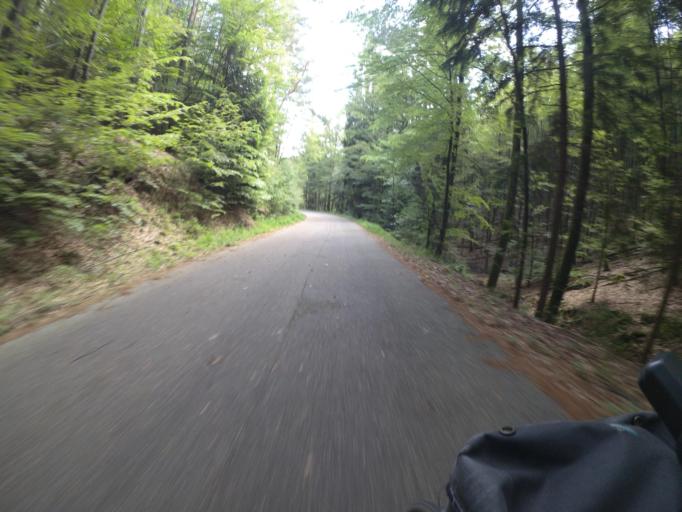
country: DE
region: Rheinland-Pfalz
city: Lemberg
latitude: 49.1450
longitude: 7.7173
